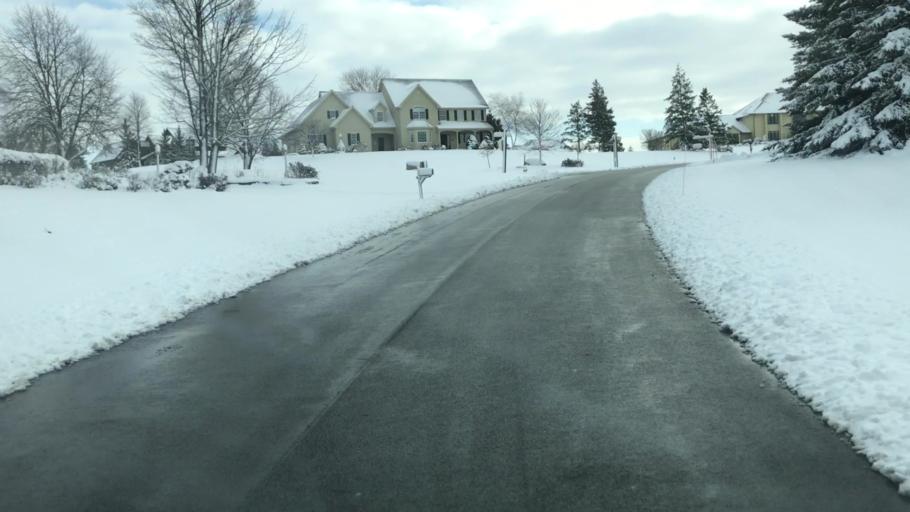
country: US
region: New York
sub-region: Onondaga County
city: Manlius
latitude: 42.9968
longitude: -75.9432
